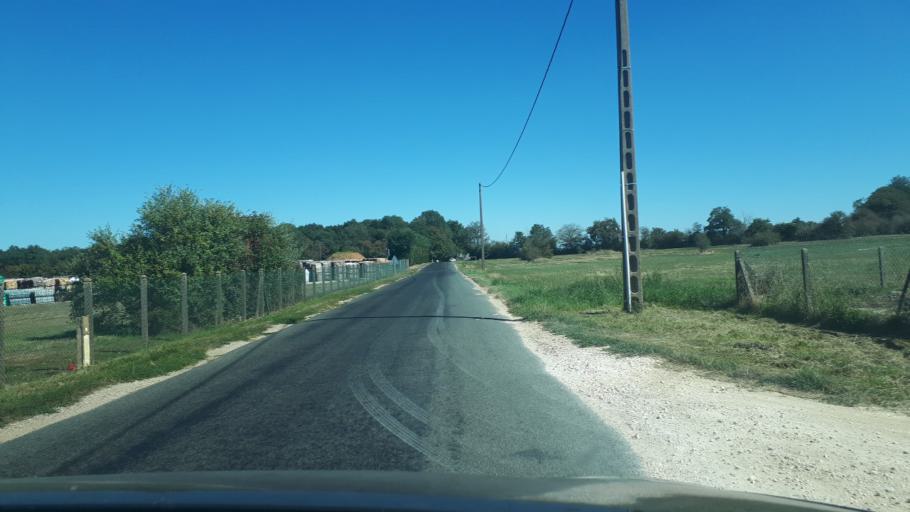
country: FR
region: Centre
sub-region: Departement du Cher
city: Sancerre
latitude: 47.3134
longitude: 2.7533
